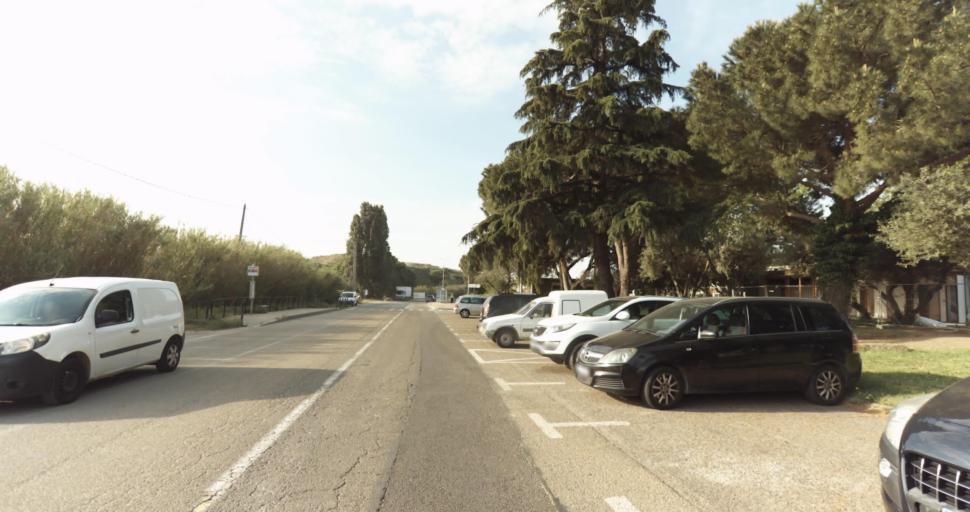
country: FR
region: Languedoc-Roussillon
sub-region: Departement du Gard
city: Rodilhan
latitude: 43.8353
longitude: 4.3944
